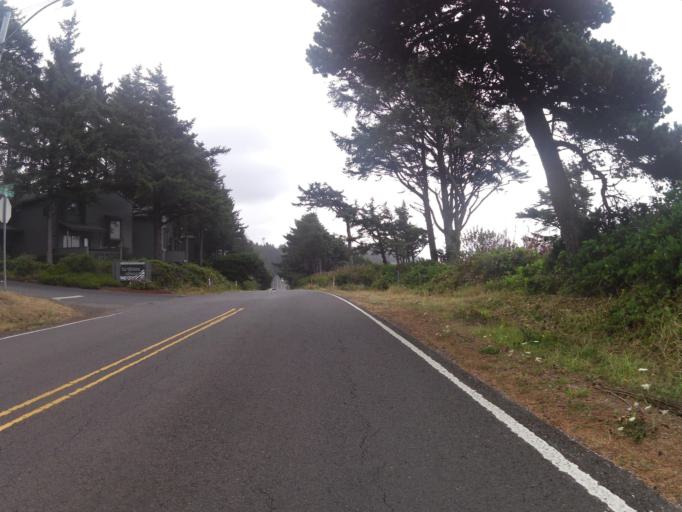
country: US
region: Oregon
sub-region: Lincoln County
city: Newport
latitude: 44.6615
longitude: -124.0570
